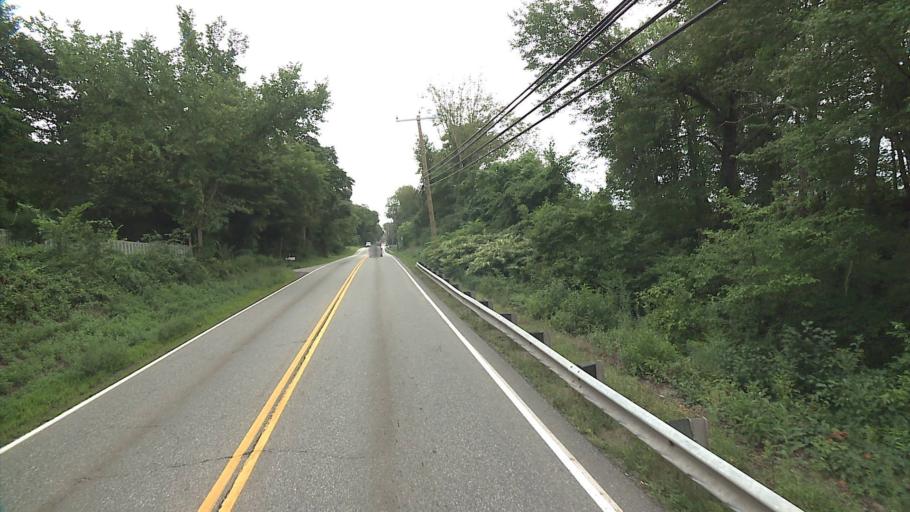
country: US
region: Connecticut
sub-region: New London County
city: Oxoboxo River
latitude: 41.4006
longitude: -72.1763
